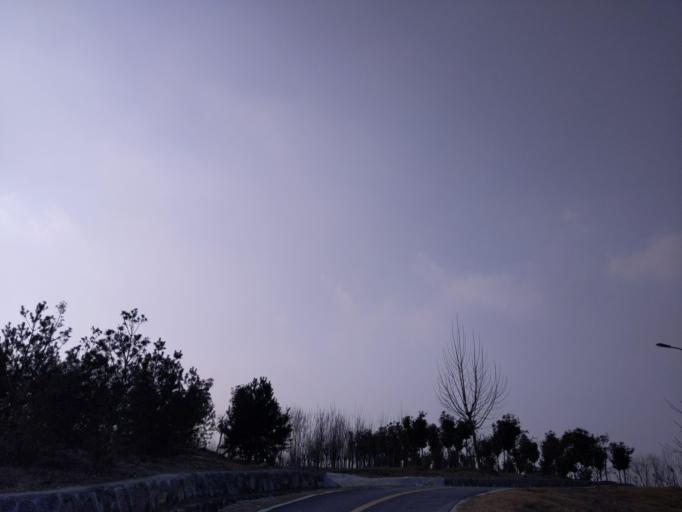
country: CN
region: Henan Sheng
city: Puyang
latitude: 35.8199
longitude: 115.0203
